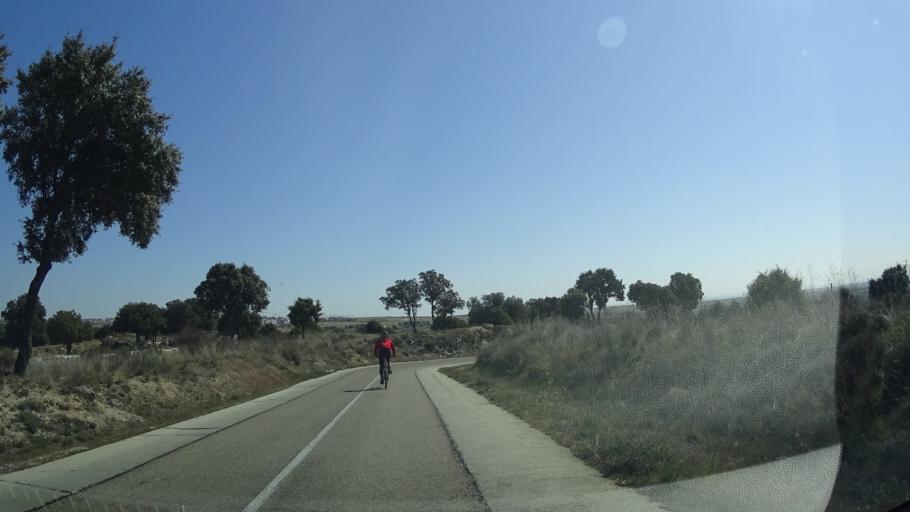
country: ES
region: Madrid
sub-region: Provincia de Madrid
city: Colmenar Viejo
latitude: 40.6443
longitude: -3.8147
